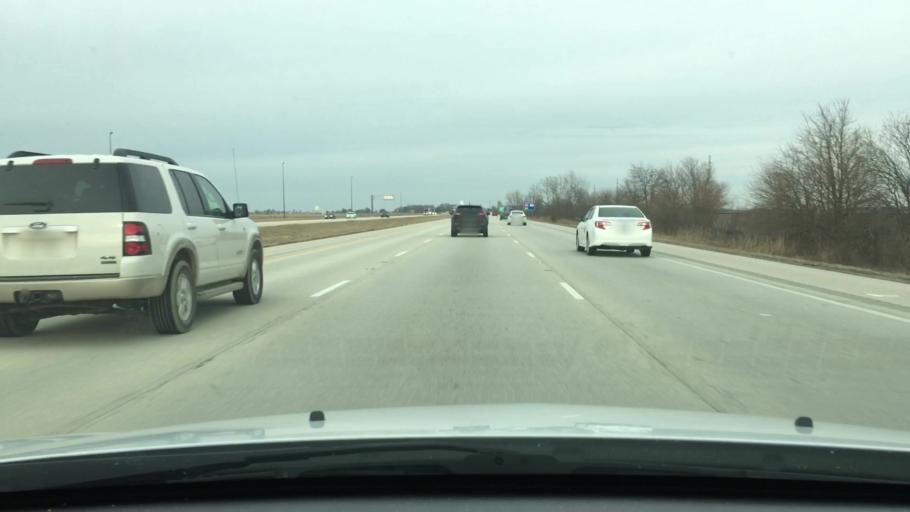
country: US
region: Illinois
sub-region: Sangamon County
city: Williamsville
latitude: 39.9315
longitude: -89.5697
